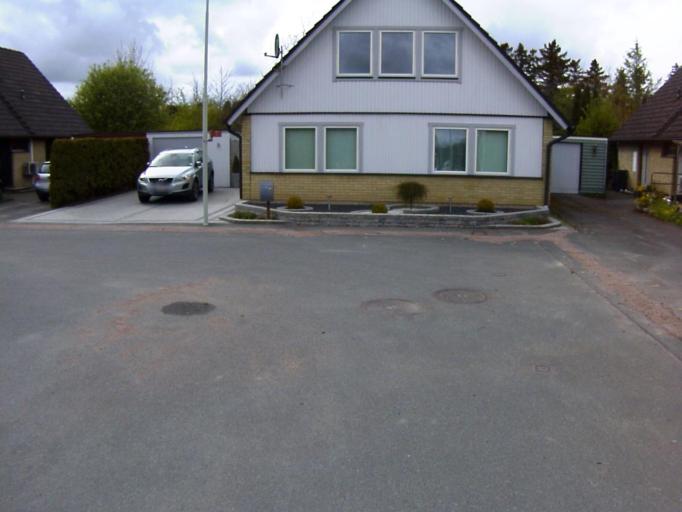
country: SE
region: Skane
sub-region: Kristianstads Kommun
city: Kristianstad
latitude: 56.0526
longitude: 14.1819
